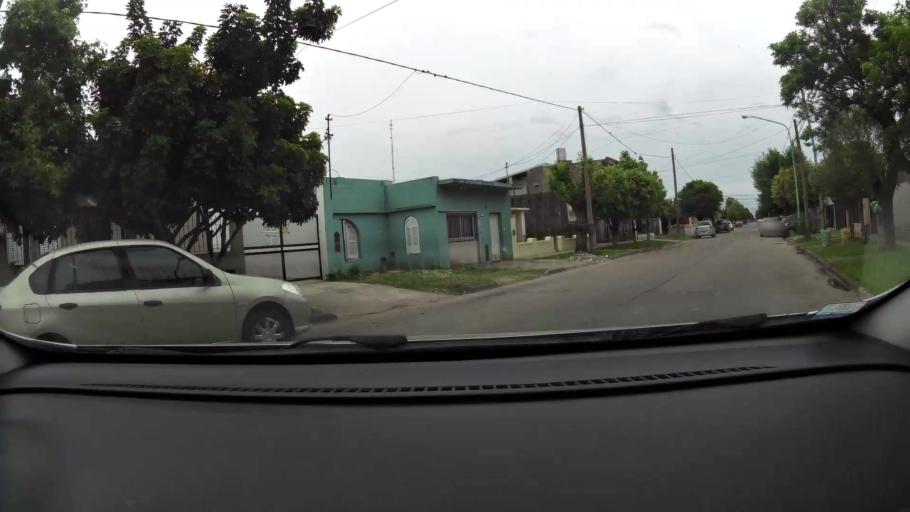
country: AR
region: Buenos Aires
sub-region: Partido de Campana
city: Campana
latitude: -34.1804
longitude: -58.9597
